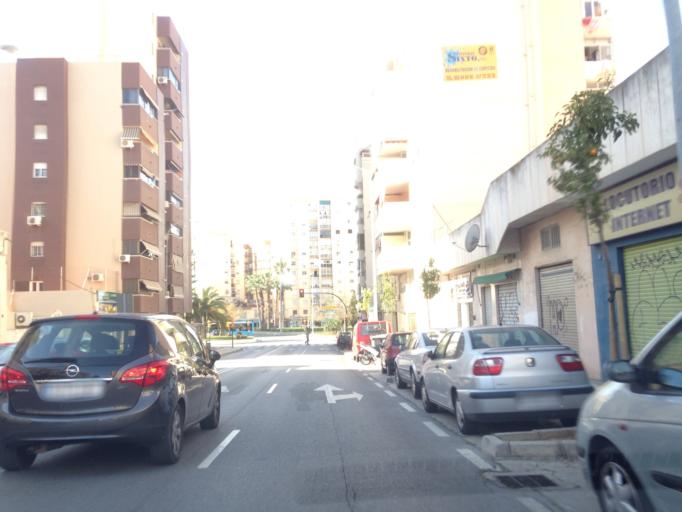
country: ES
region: Andalusia
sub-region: Provincia de Malaga
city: Malaga
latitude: 36.7226
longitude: -4.4398
